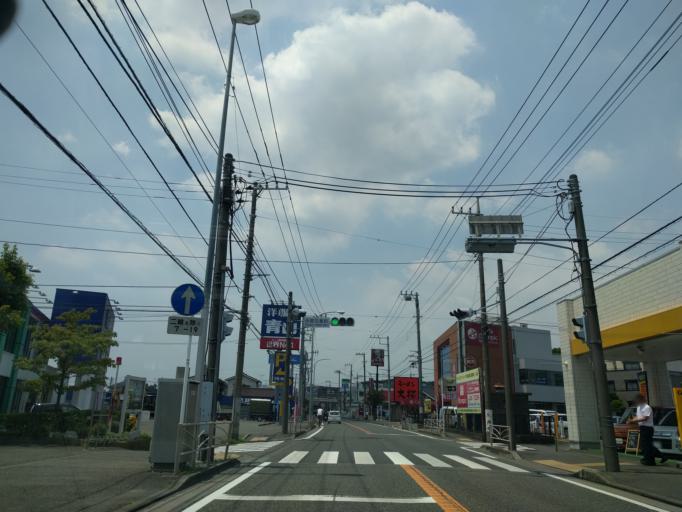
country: JP
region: Kanagawa
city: Minami-rinkan
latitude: 35.4817
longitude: 139.5326
